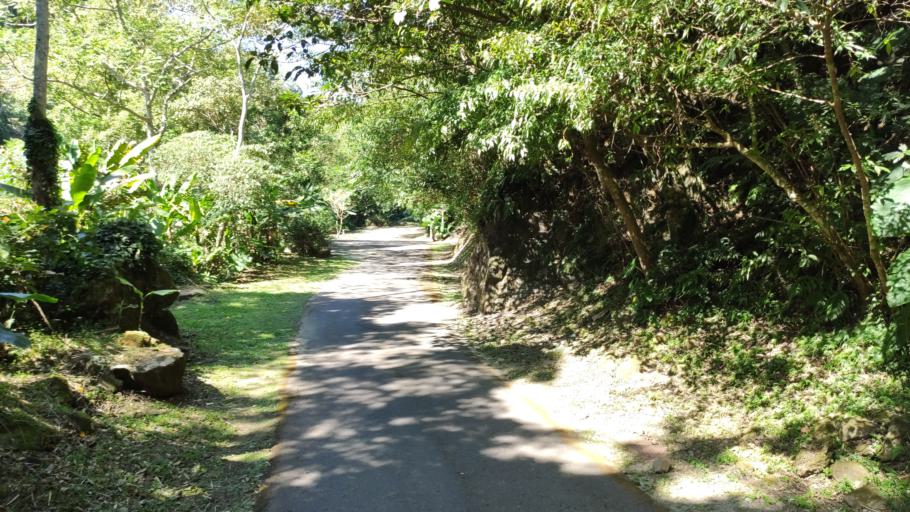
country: TW
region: Taiwan
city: Daxi
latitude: 24.8421
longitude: 121.3047
